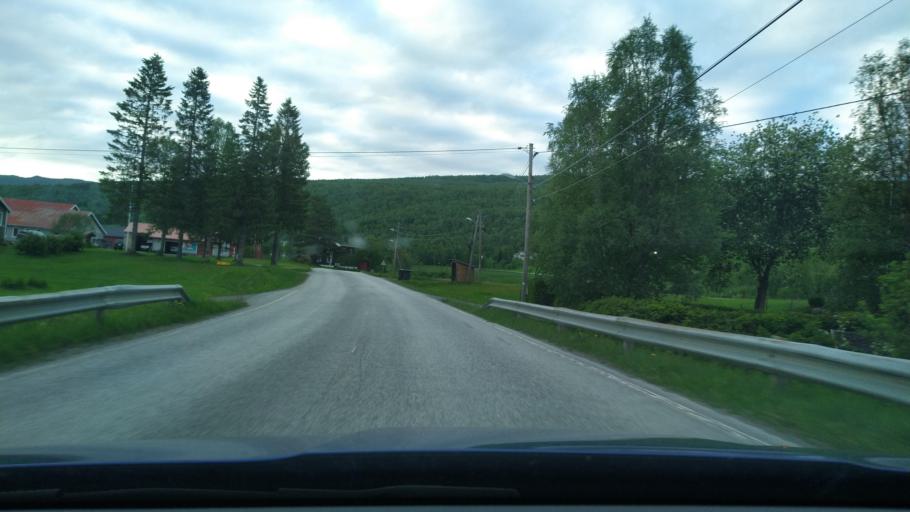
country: NO
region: Troms
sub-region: Sorreisa
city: Sorreisa
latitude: 69.1185
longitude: 18.2175
